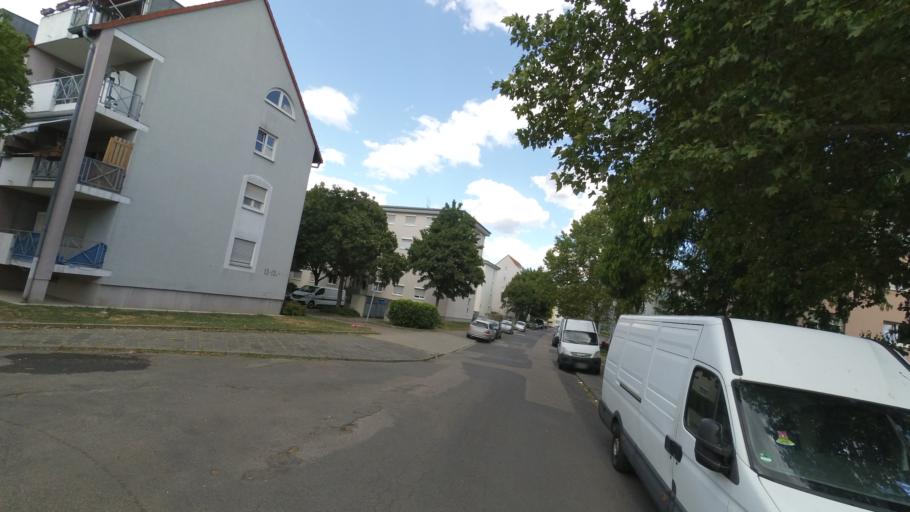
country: DE
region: Baden-Wuerttemberg
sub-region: Karlsruhe Region
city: Mannheim
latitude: 49.5046
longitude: 8.4645
